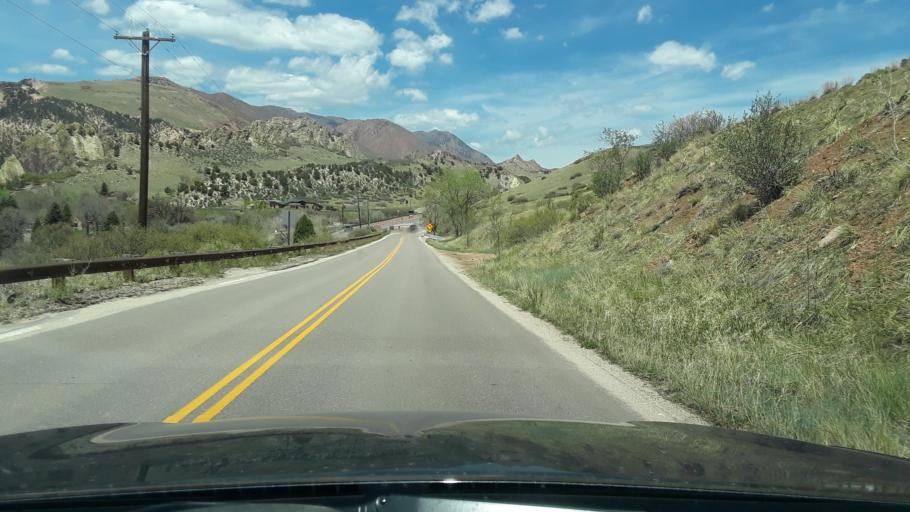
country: US
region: Colorado
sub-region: El Paso County
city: Manitou Springs
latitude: 38.8864
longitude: -104.8740
